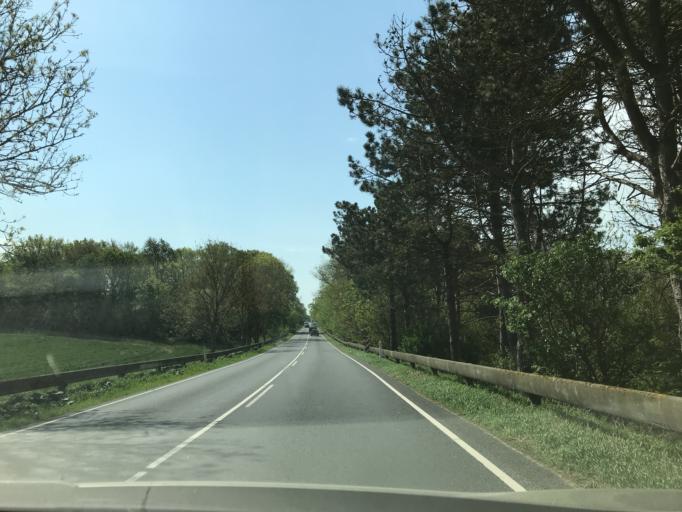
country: DK
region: South Denmark
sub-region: Assens Kommune
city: Assens
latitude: 55.3450
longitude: 9.9373
